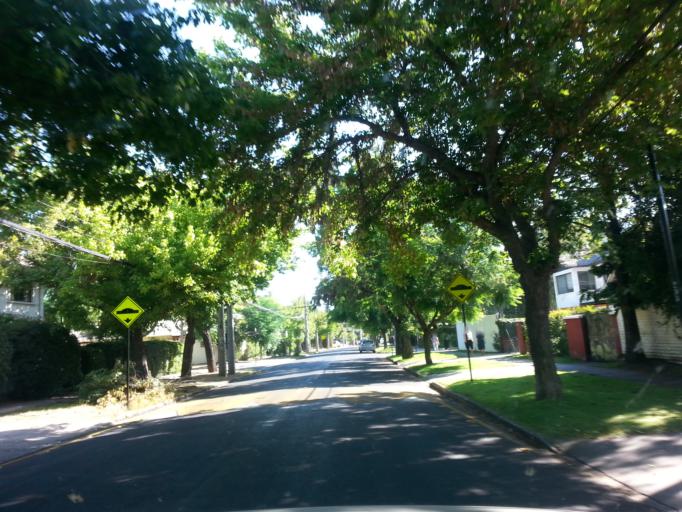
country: CL
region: Santiago Metropolitan
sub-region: Provincia de Santiago
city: Villa Presidente Frei, Nunoa, Santiago, Chile
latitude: -33.3917
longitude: -70.5875
